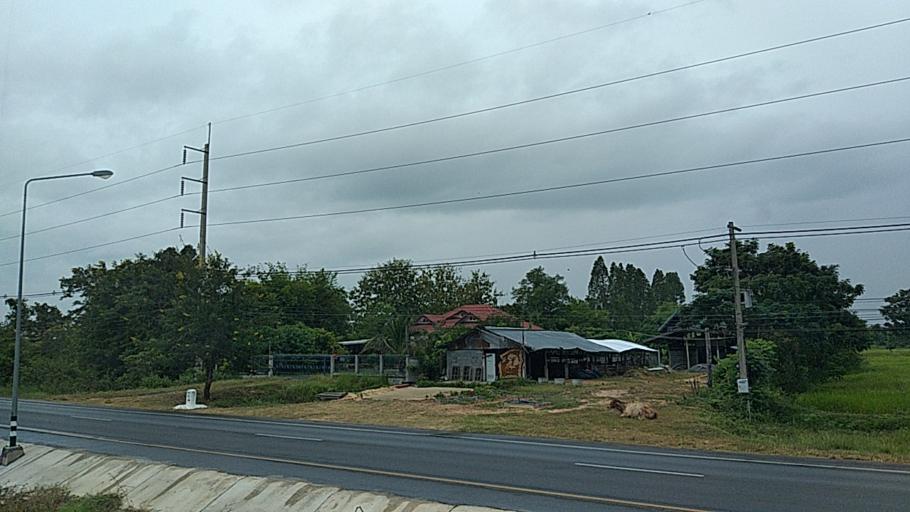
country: TH
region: Maha Sarakham
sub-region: Amphoe Borabue
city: Borabue
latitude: 16.0641
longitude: 103.1421
